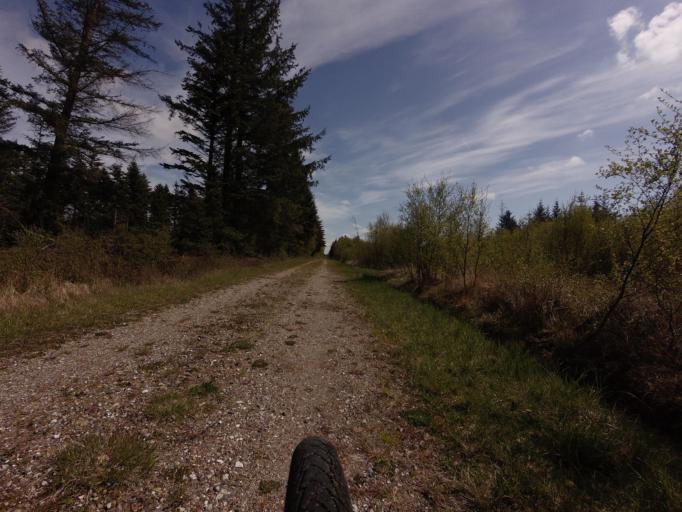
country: DK
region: North Denmark
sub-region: Jammerbugt Kommune
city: Brovst
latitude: 57.1692
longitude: 9.5474
